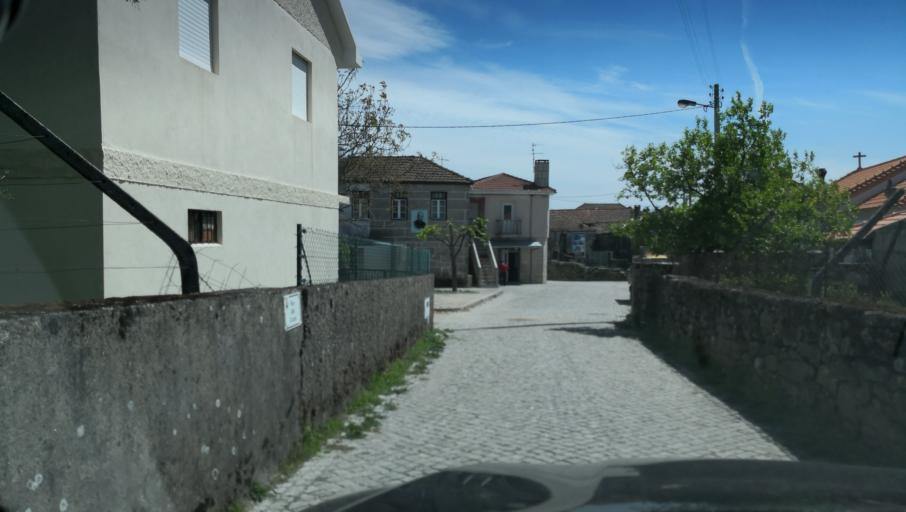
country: PT
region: Vila Real
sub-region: Vila Real
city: Vila Real
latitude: 41.3577
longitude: -7.6988
